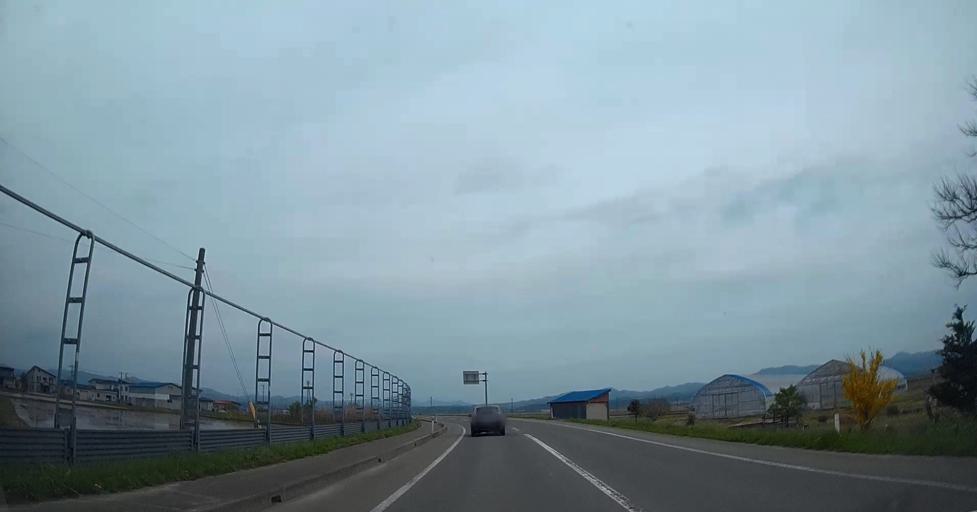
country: JP
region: Aomori
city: Shimokizukuri
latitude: 40.9787
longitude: 140.3750
